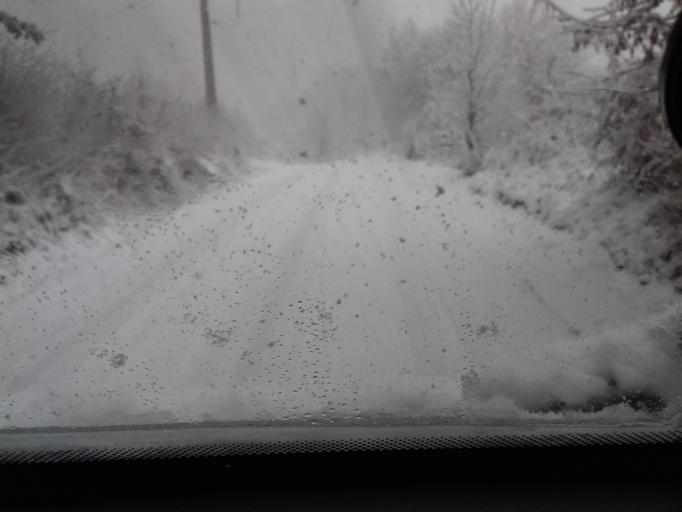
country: BA
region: Federation of Bosnia and Herzegovina
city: Lokvine
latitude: 44.2406
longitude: 17.8128
